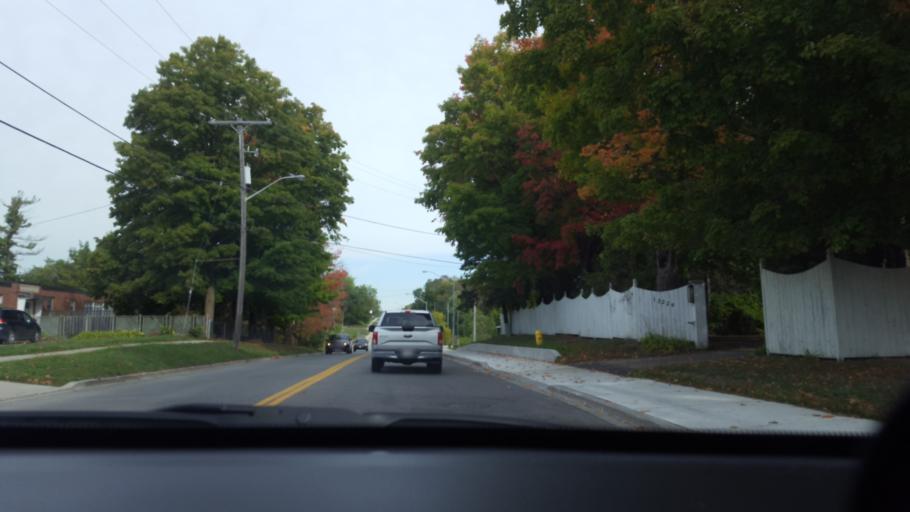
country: CA
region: Ontario
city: Vaughan
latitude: 43.9336
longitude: -79.5295
